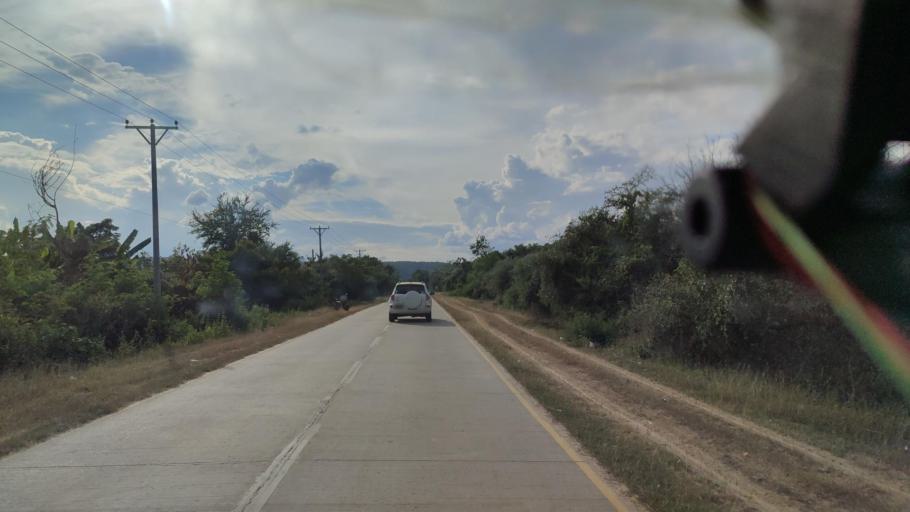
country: MM
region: Mandalay
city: Yamethin
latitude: 20.1550
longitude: 96.1333
